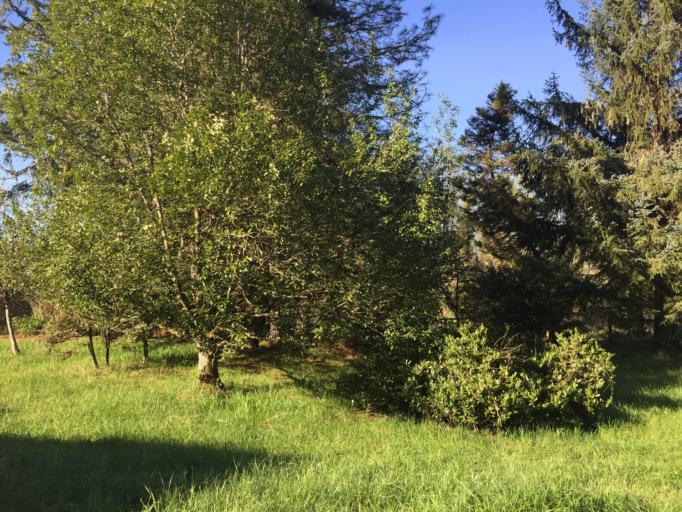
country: US
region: Oregon
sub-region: Lane County
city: Springfield
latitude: 44.0037
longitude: -122.9806
